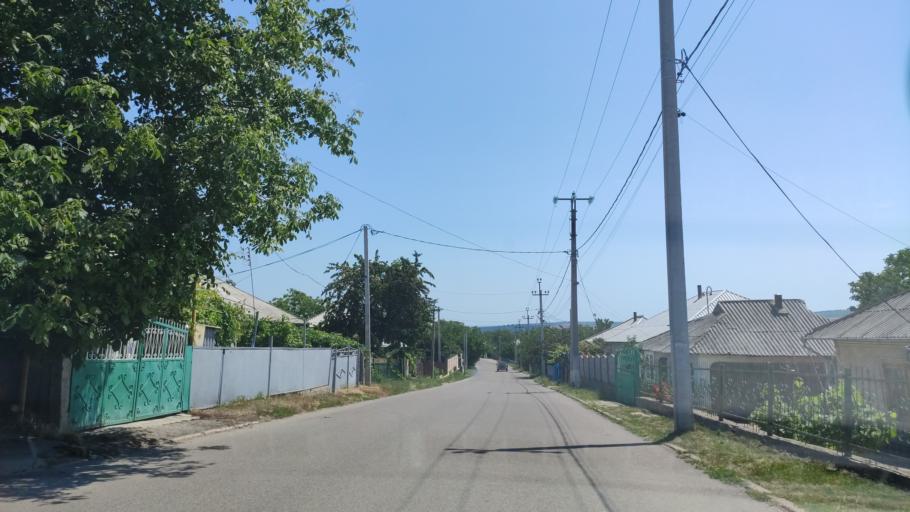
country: MD
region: Raionul Soroca
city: Soroca
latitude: 48.1483
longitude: 28.2807
